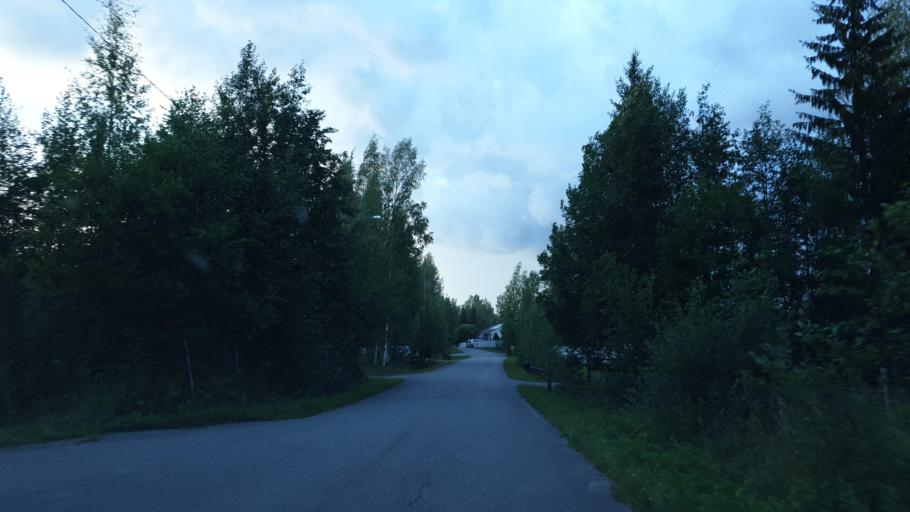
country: FI
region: Northern Savo
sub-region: Varkaus
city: Leppaevirta
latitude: 62.5823
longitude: 27.6227
